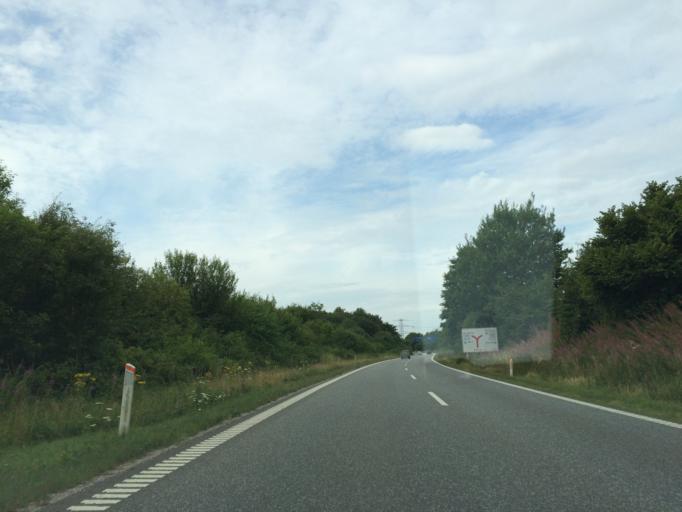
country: DK
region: South Denmark
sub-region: Kolding Kommune
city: Kolding
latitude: 55.5366
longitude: 9.5045
